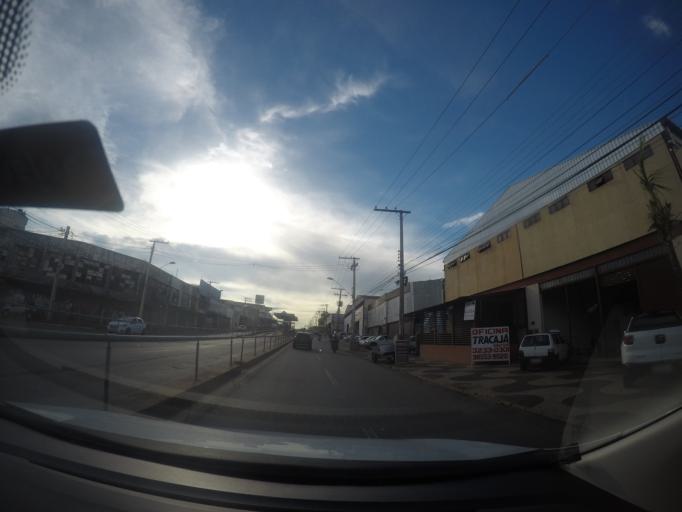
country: BR
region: Goias
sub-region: Goiania
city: Goiania
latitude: -16.6699
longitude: -49.2990
